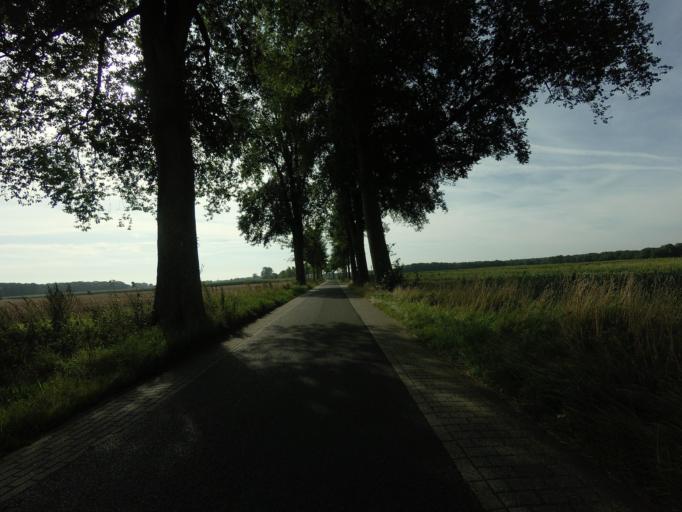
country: NL
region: Drenthe
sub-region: Gemeente Assen
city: Assen
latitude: 53.0039
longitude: 6.6223
